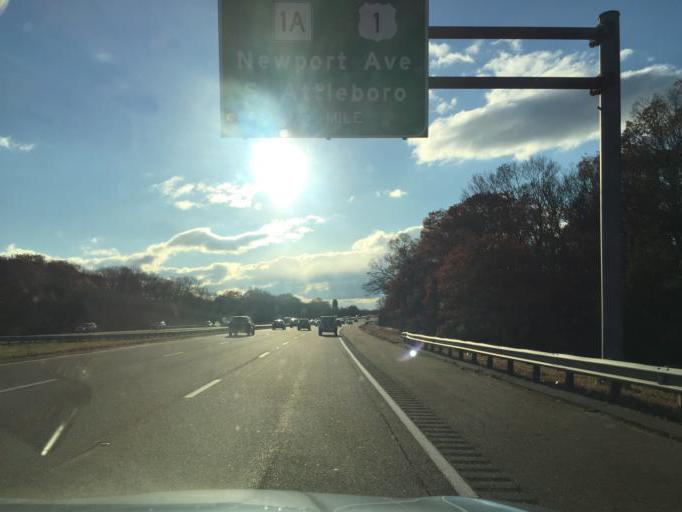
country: US
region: Massachusetts
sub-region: Bristol County
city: North Seekonk
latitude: 41.9067
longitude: -71.3448
